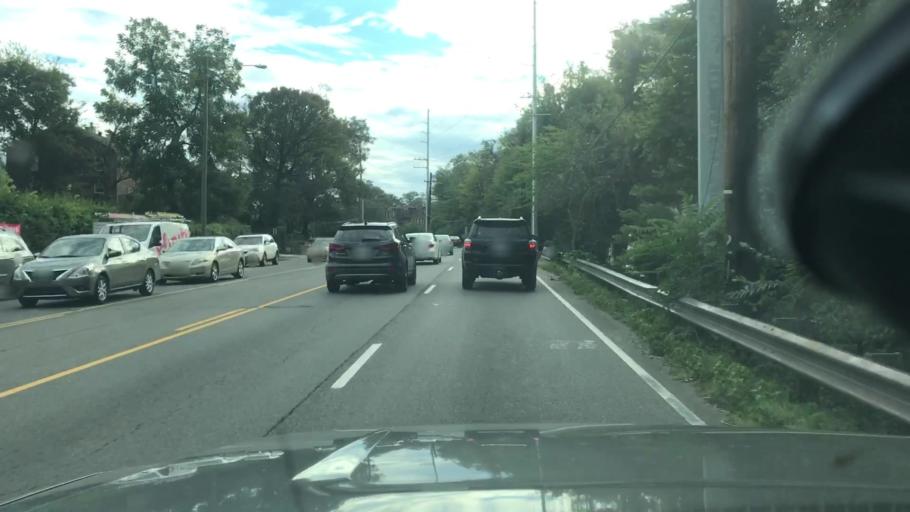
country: US
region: Tennessee
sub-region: Davidson County
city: Oak Hill
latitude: 36.1185
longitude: -86.8097
